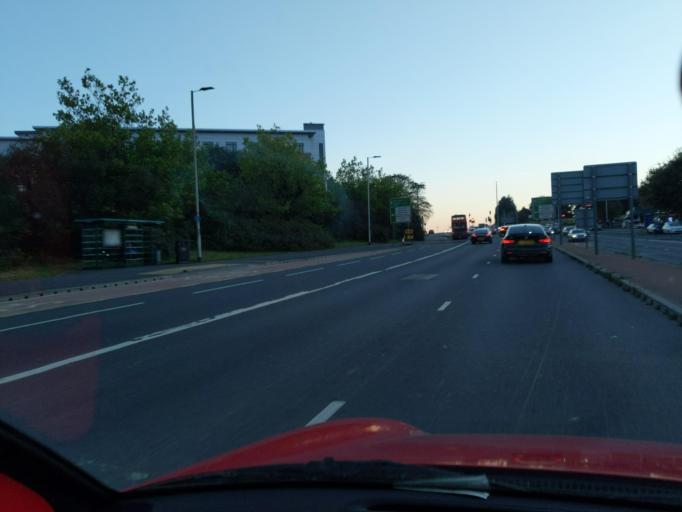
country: GB
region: England
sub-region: Plymouth
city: Plymouth
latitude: 50.4152
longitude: -4.1257
